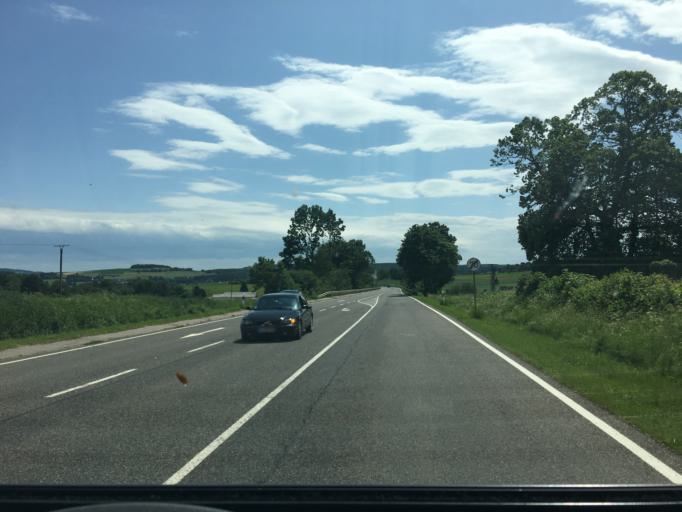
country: DE
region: North Rhine-Westphalia
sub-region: Regierungsbezirk Koln
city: Mechernich
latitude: 50.5639
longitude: 6.7024
